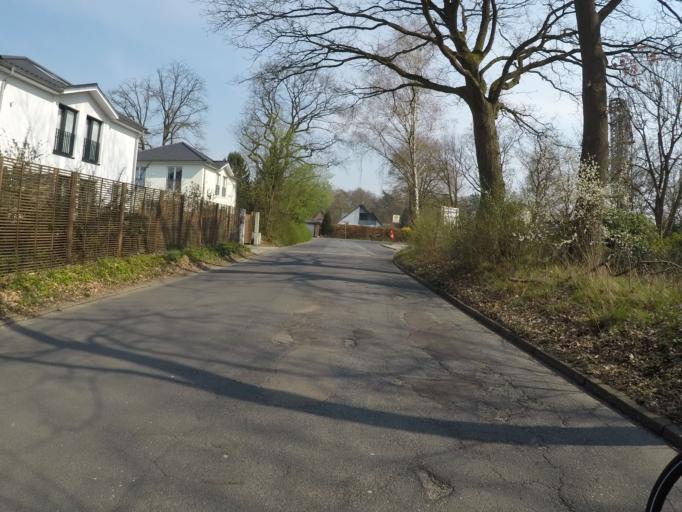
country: DE
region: Hamburg
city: Sasel
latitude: 53.6649
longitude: 10.1056
